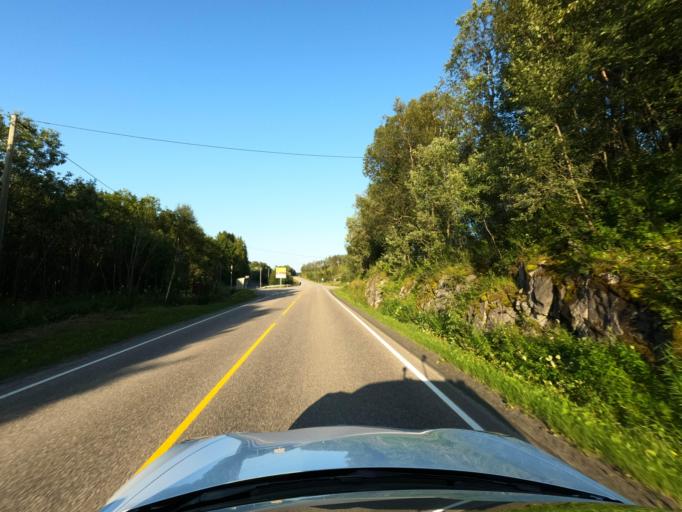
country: NO
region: Troms
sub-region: Skanland
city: Evenskjer
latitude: 68.4926
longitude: 16.7290
